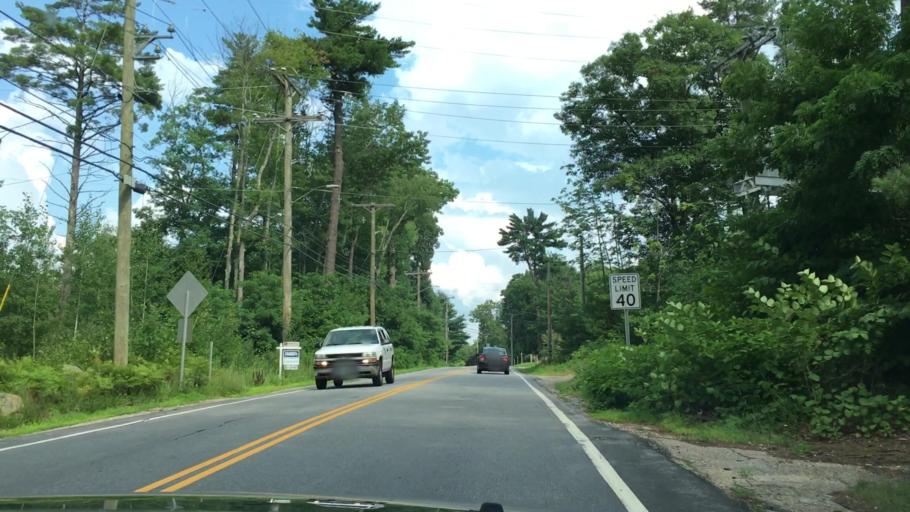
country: US
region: New Hampshire
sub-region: Belknap County
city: Gilford
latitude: 43.6024
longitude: -71.4499
